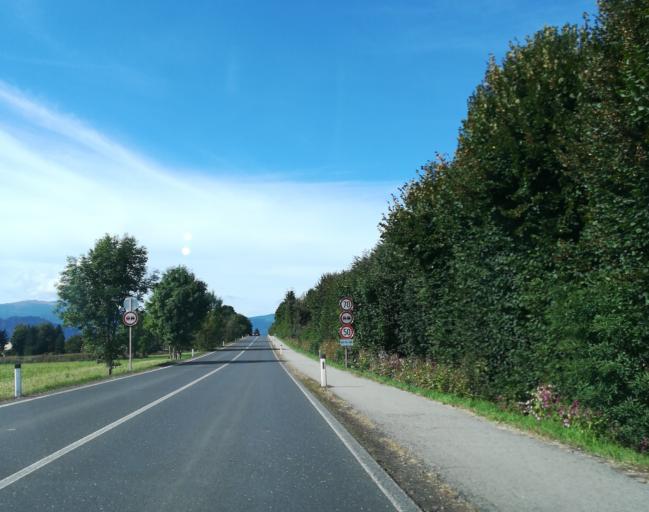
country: AT
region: Styria
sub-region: Politischer Bezirk Murtal
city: Zeltweg
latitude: 47.1961
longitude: 14.7588
